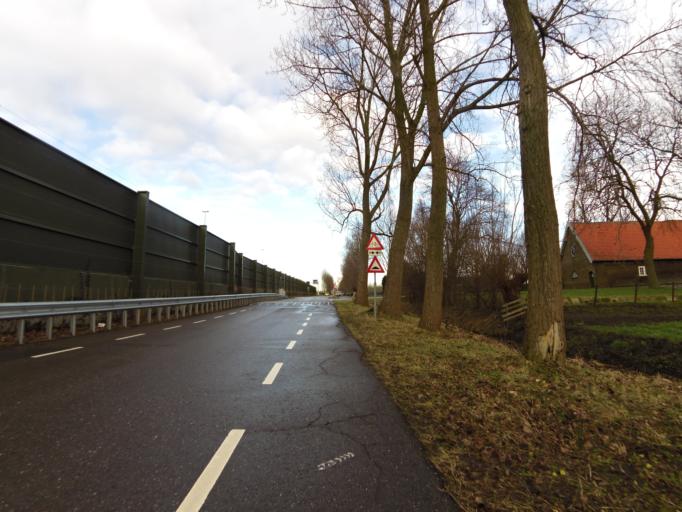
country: NL
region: South Holland
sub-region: Gemeente Delft
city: Delft
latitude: 51.9777
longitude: 4.3974
